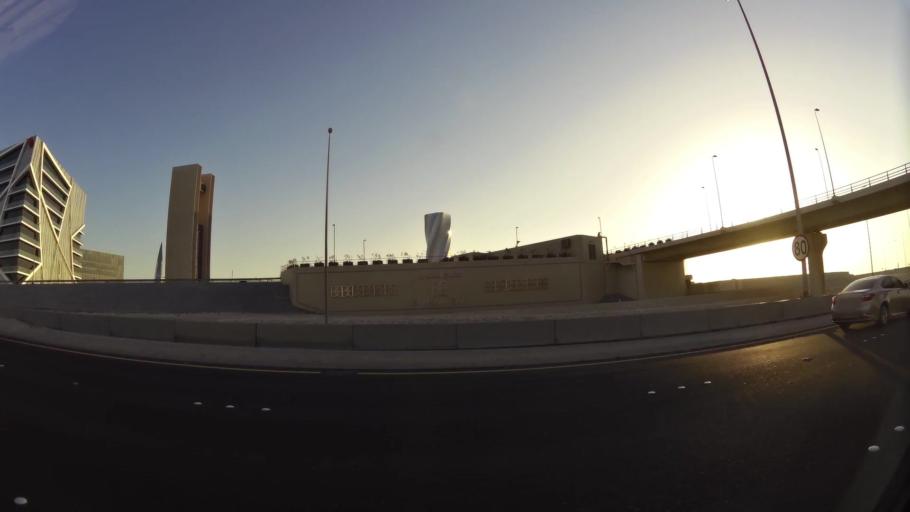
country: BH
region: Muharraq
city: Al Muharraq
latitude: 26.2526
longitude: 50.5823
